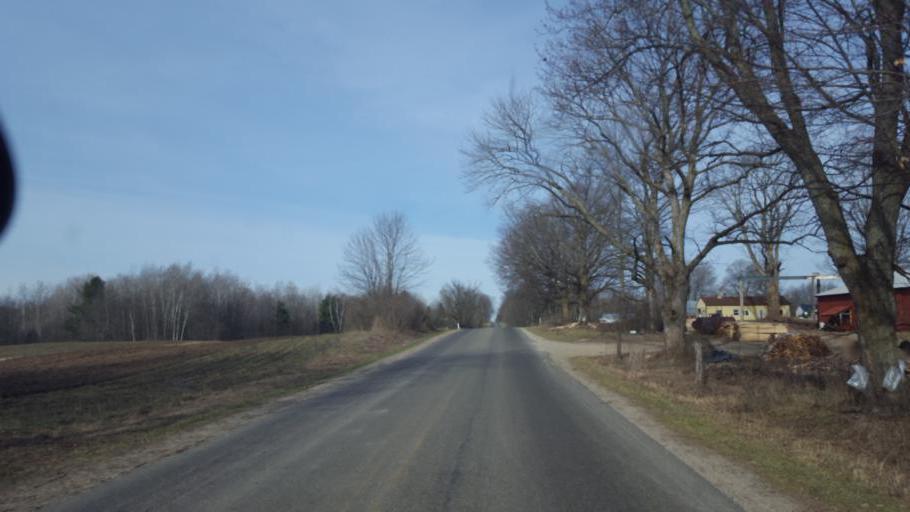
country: US
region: Michigan
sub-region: Montcalm County
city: Howard City
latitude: 43.5261
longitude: -85.4580
